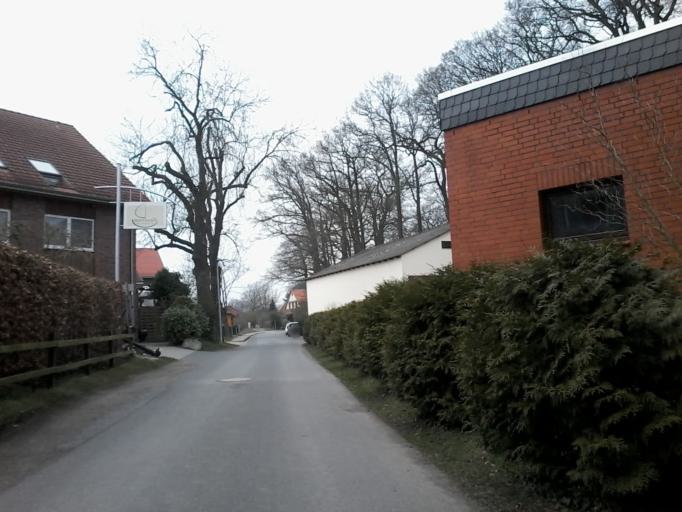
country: DE
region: Lower Saxony
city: Achim
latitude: 52.9975
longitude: 9.0503
